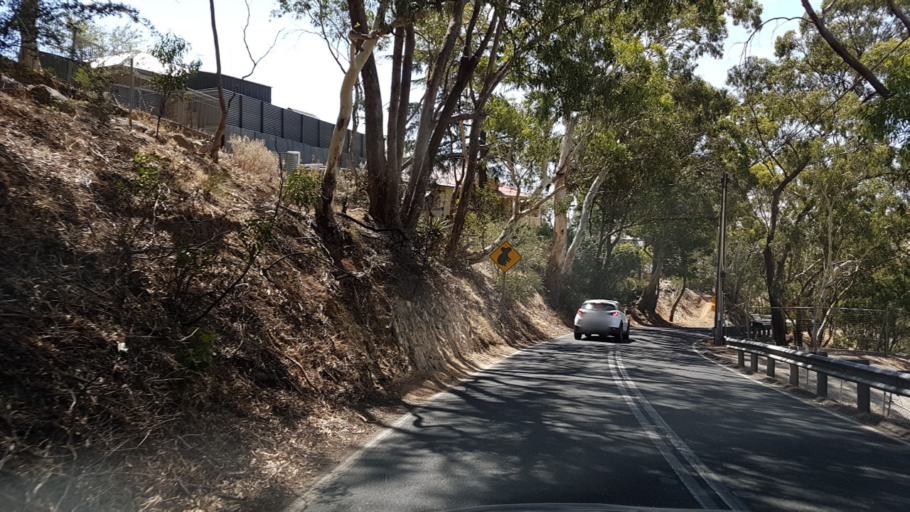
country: AU
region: South Australia
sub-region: Mitcham
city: Belair
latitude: -34.9964
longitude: 138.6296
